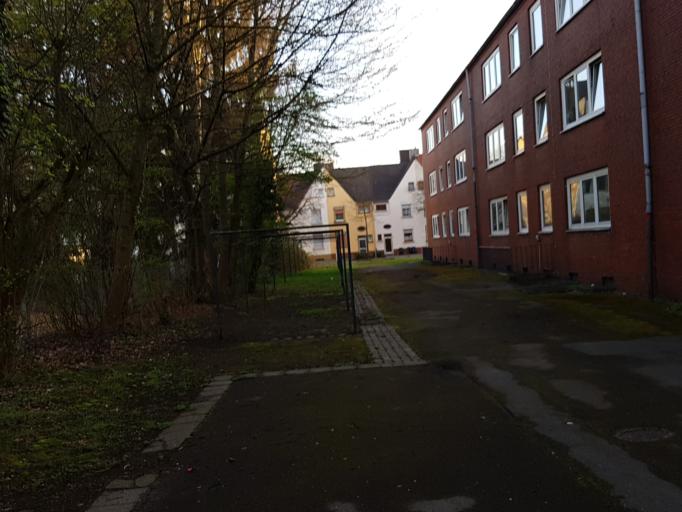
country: DE
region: North Rhine-Westphalia
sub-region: Regierungsbezirk Koln
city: Wurselen
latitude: 50.7762
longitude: 6.1375
